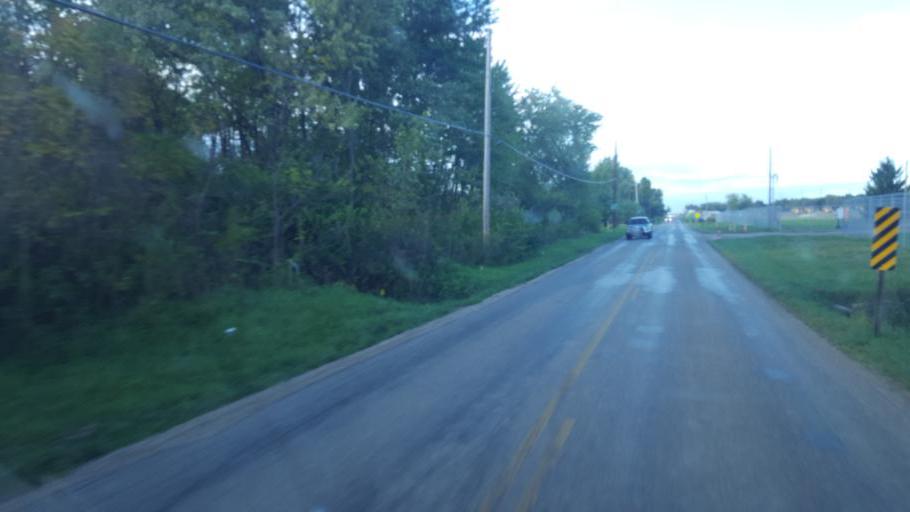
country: US
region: Ohio
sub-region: Franklin County
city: New Albany
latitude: 40.0643
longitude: -82.7546
